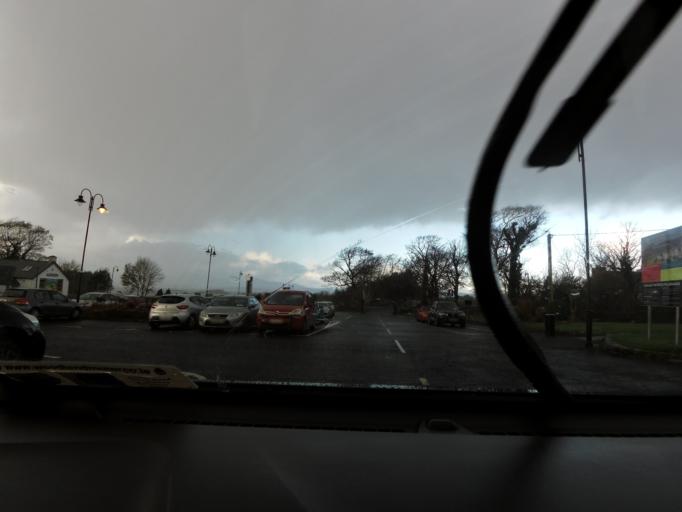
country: IE
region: Connaught
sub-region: Maigh Eo
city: Westport
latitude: 53.7792
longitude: -9.6400
